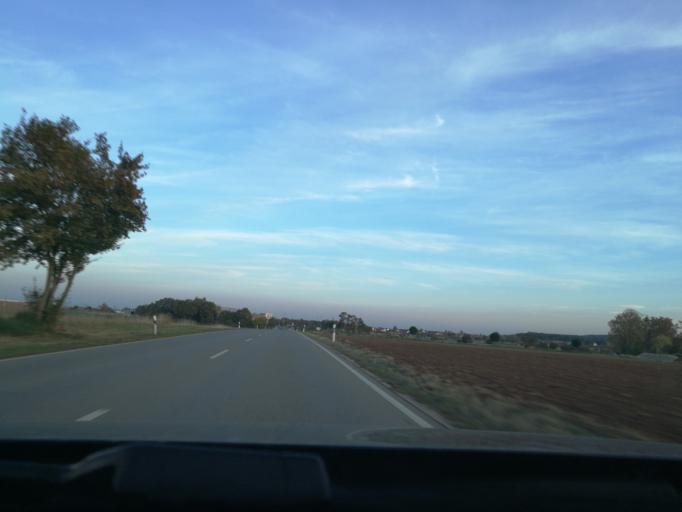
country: DE
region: Bavaria
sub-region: Regierungsbezirk Mittelfranken
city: Veitsbronn
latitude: 49.4987
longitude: 10.8986
